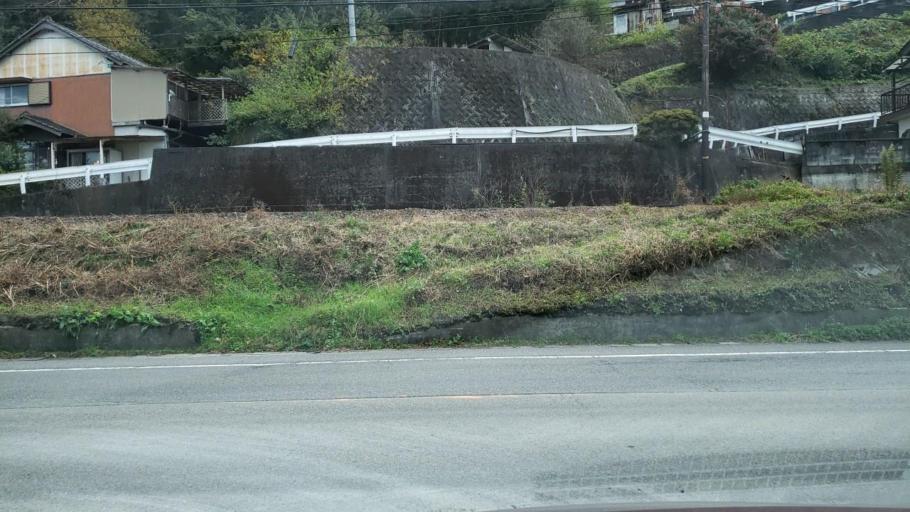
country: JP
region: Tokushima
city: Wakimachi
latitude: 34.0561
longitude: 134.1554
